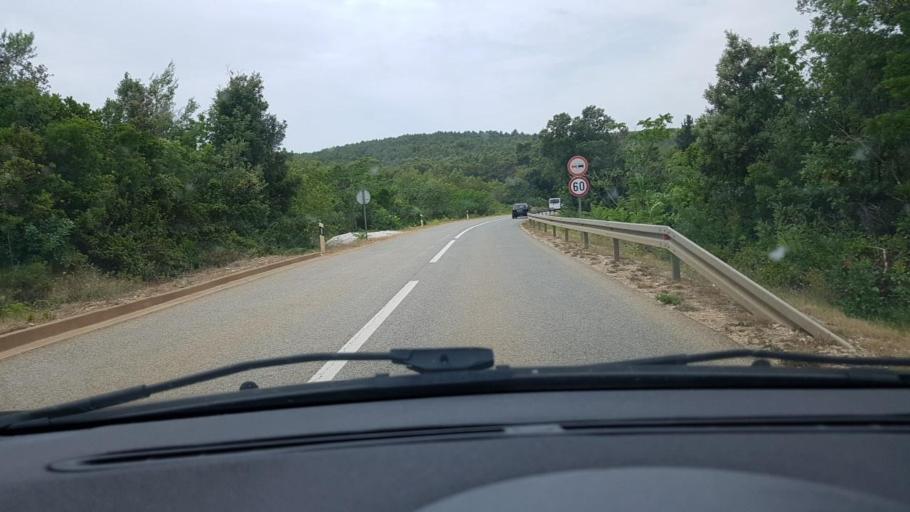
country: HR
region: Dubrovacko-Neretvanska
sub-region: Grad Korcula
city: Zrnovo
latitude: 42.9368
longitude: 17.0835
